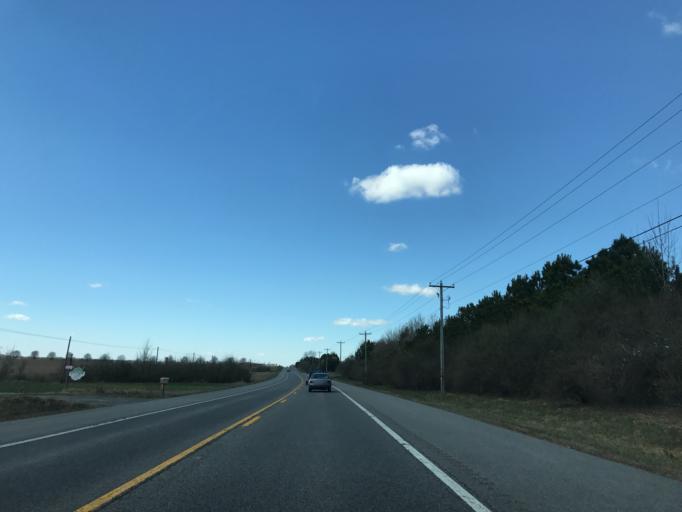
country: US
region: Maryland
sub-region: Queen Anne's County
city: Kingstown
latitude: 39.1835
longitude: -76.0086
